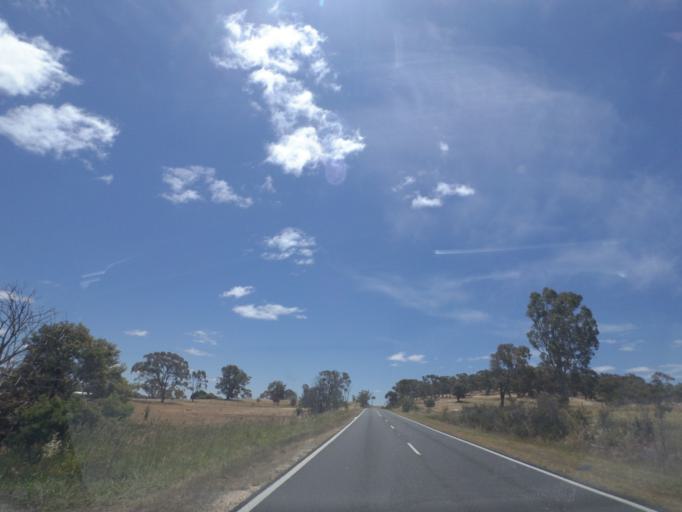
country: AU
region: Victoria
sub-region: Mount Alexander
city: Castlemaine
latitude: -37.2169
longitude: 144.1406
